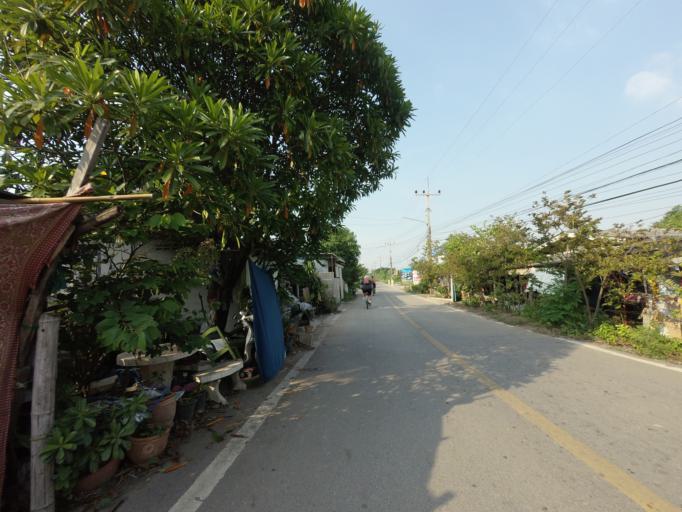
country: TH
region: Samut Sakhon
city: Samut Sakhon
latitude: 13.5084
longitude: 100.3069
